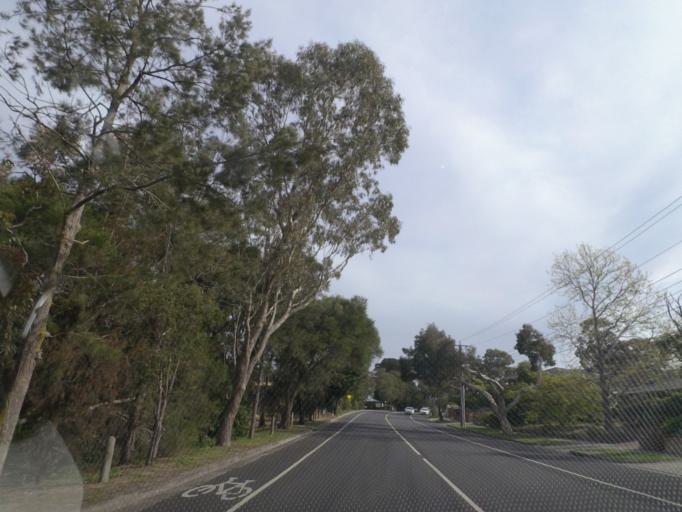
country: AU
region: Victoria
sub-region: Knox
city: Wantirna
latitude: -37.8532
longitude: 145.2021
